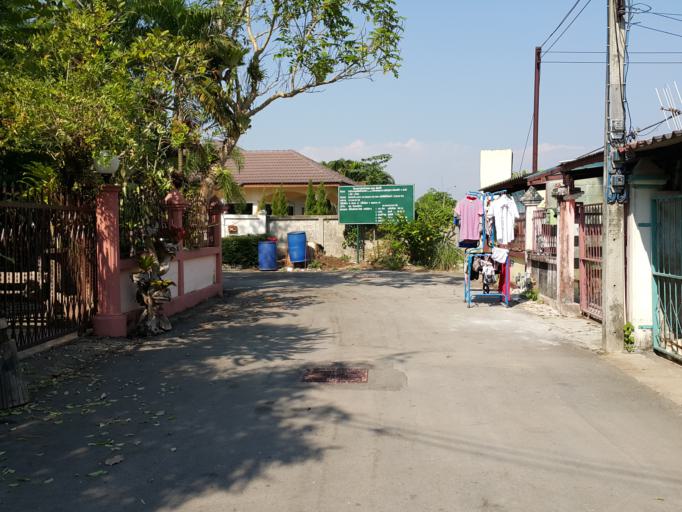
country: TH
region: Lampang
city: Lampang
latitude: 18.3061
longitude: 99.4912
